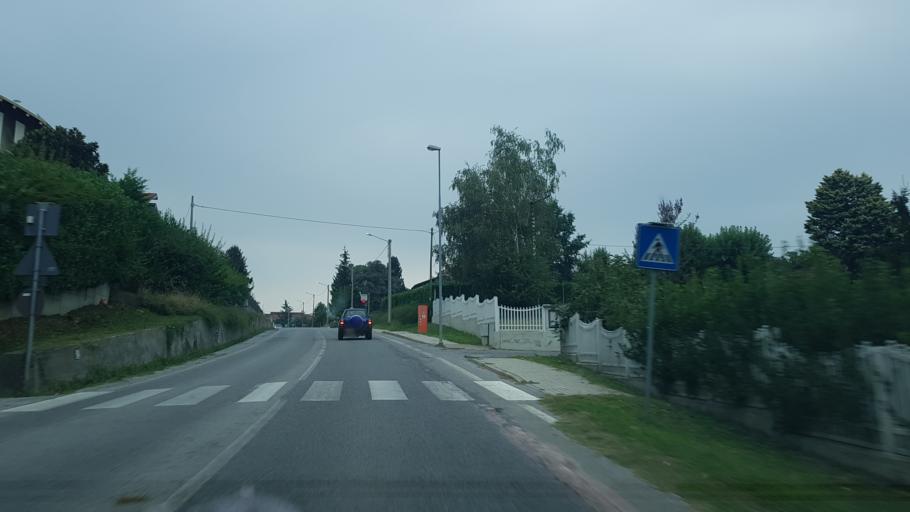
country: IT
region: Piedmont
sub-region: Provincia di Cuneo
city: Villanova Mondovi
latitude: 44.3446
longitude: 7.7775
